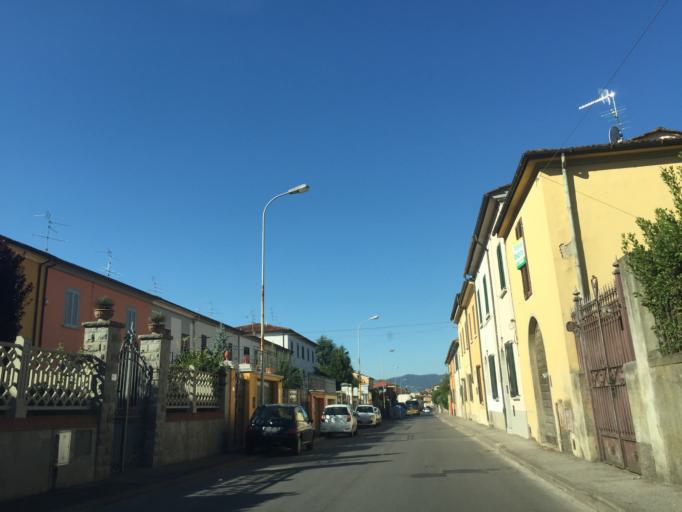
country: IT
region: Tuscany
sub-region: Provincia di Pistoia
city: Pistoia
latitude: 43.9422
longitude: 10.9285
